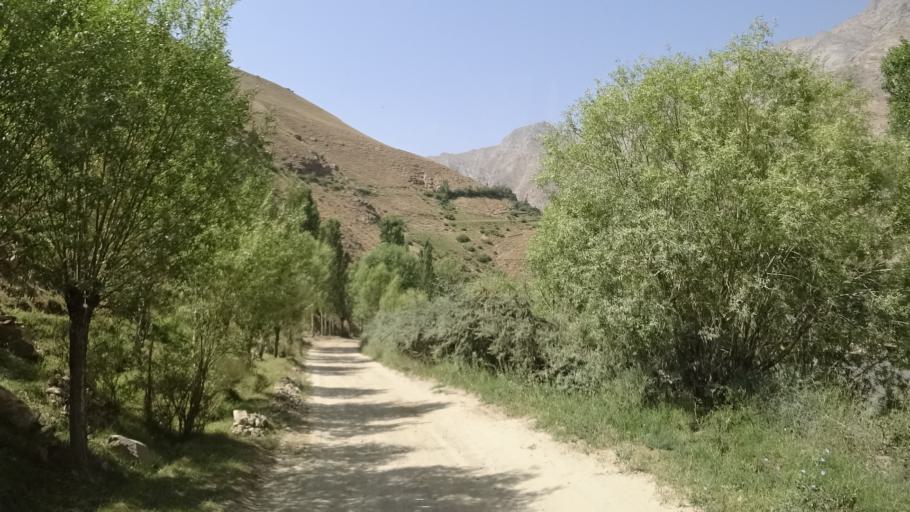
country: TJ
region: Gorno-Badakhshan
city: Khorugh
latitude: 37.1826
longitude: 71.4585
